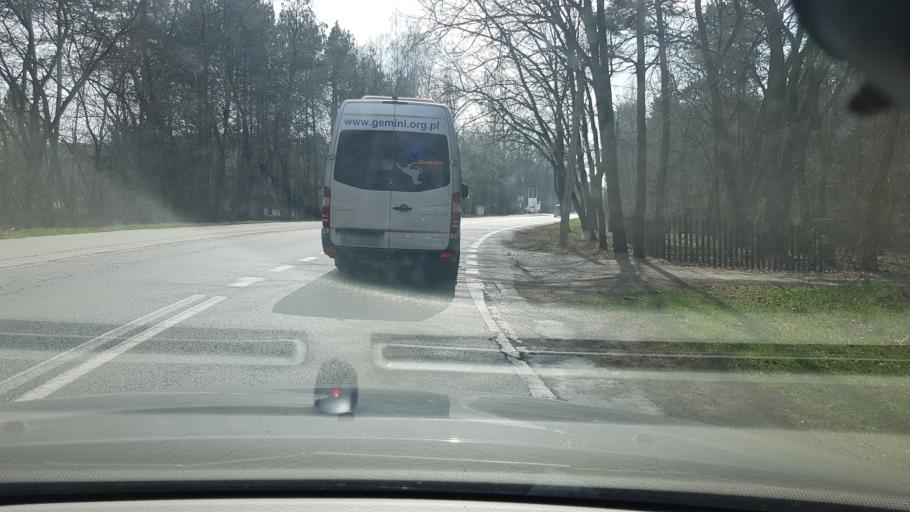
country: PL
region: Masovian Voivodeship
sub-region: Warszawa
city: Wesola
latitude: 52.2342
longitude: 21.2244
